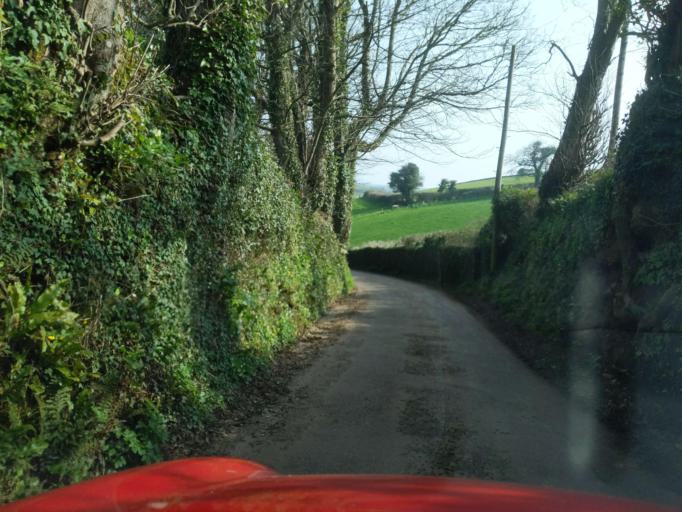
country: GB
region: England
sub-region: Devon
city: Kingsbridge
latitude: 50.2863
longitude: -3.7261
